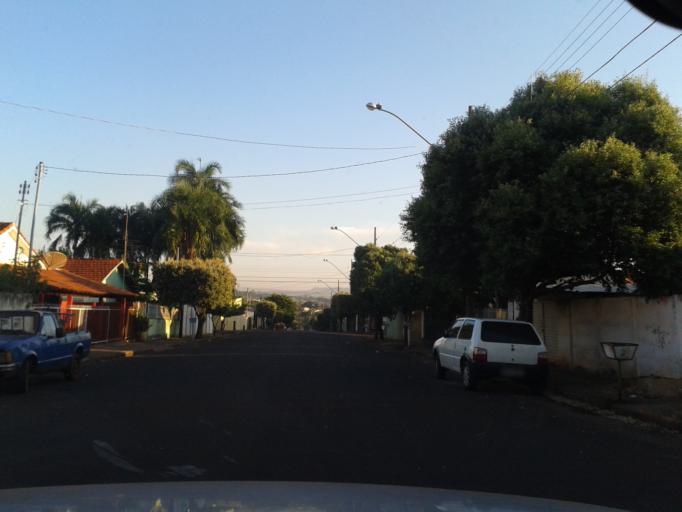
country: BR
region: Minas Gerais
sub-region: Ituiutaba
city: Ituiutaba
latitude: -18.9814
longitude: -49.4681
